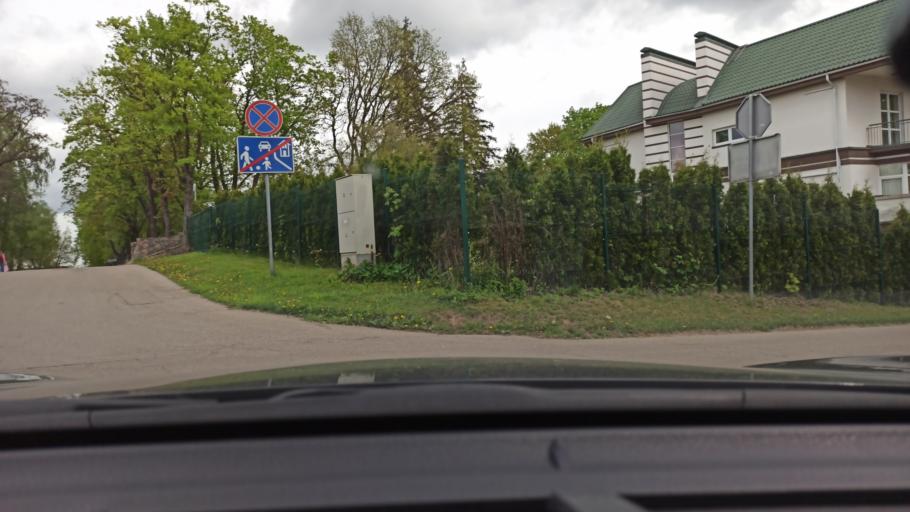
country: LT
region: Siauliu apskritis
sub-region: Siauliai
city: Siauliai
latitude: 55.9354
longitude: 23.3033
